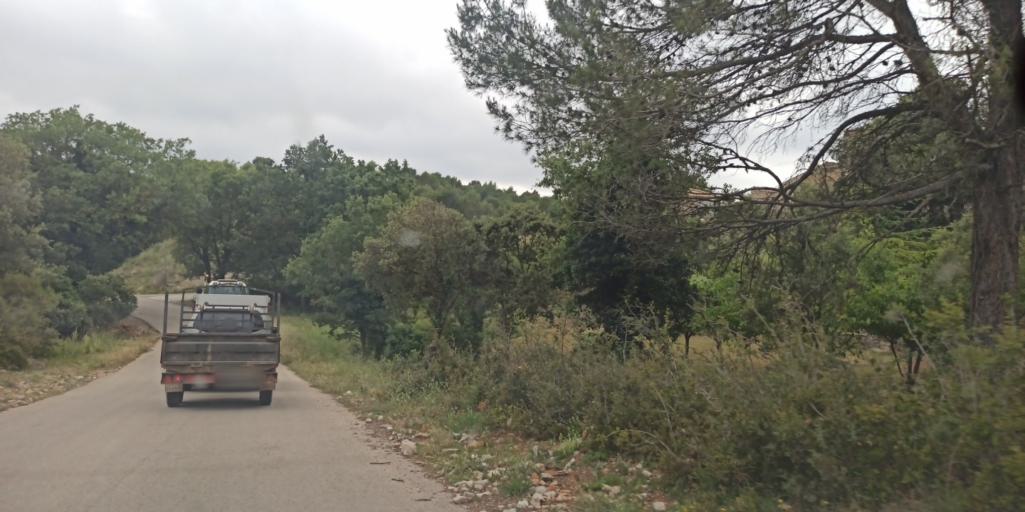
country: ES
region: Catalonia
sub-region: Provincia de Tarragona
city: Querol
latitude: 41.4209
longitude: 1.4996
